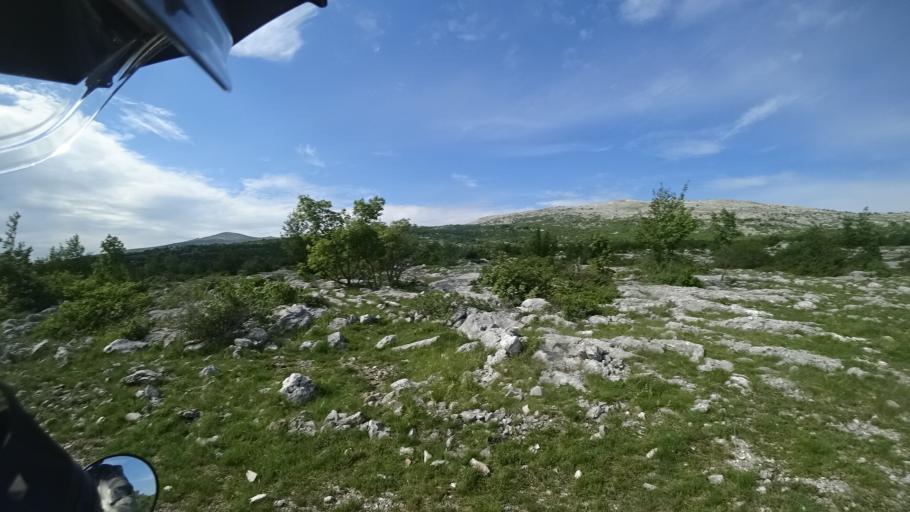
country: HR
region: Splitsko-Dalmatinska
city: Hrvace
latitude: 43.7802
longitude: 16.4448
